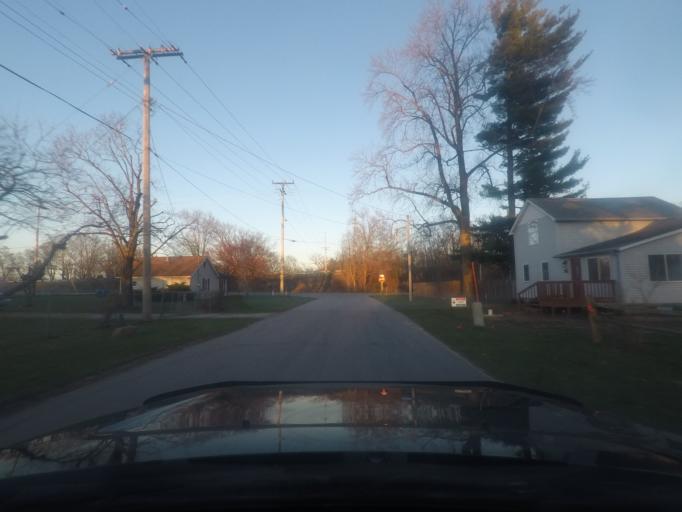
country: US
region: Indiana
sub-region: LaPorte County
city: Kingsford Heights
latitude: 41.5244
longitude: -86.6995
